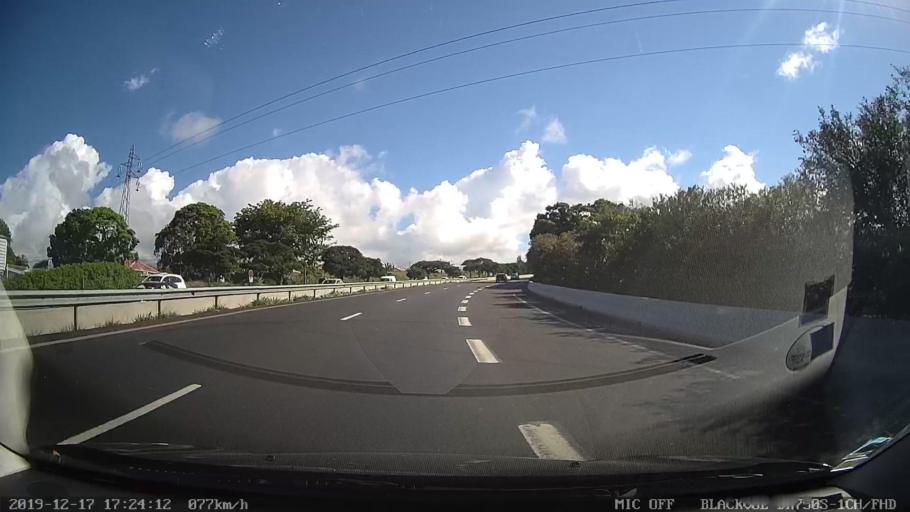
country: RE
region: Reunion
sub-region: Reunion
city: Le Tampon
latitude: -21.3041
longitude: 55.4995
